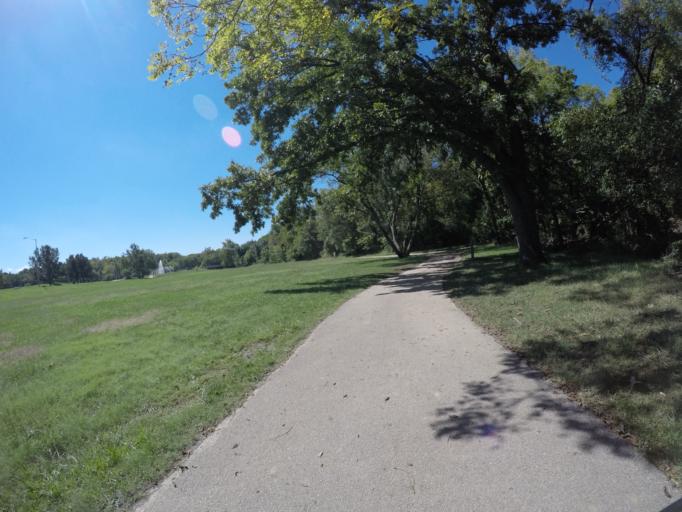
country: US
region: Kansas
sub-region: Johnson County
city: Lenexa
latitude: 38.9328
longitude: -94.6961
